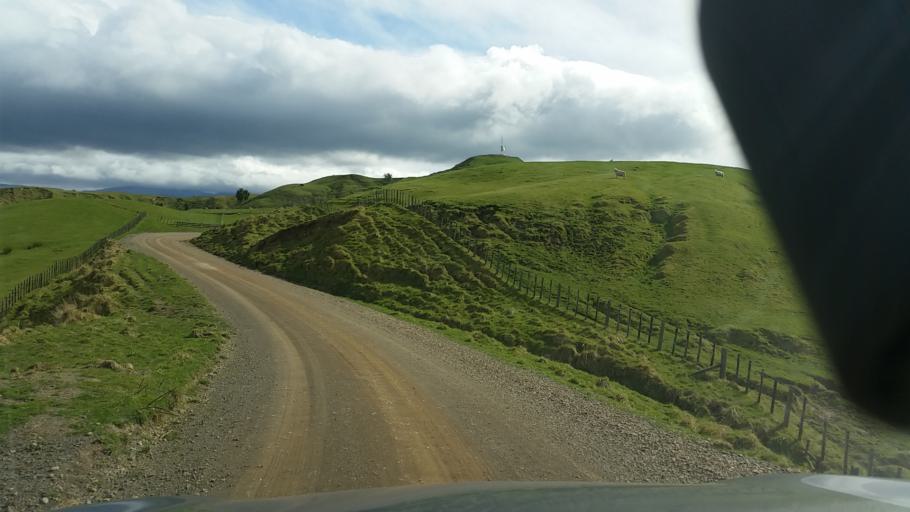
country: NZ
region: Hawke's Bay
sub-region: Napier City
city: Napier
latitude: -39.2070
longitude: 176.9560
